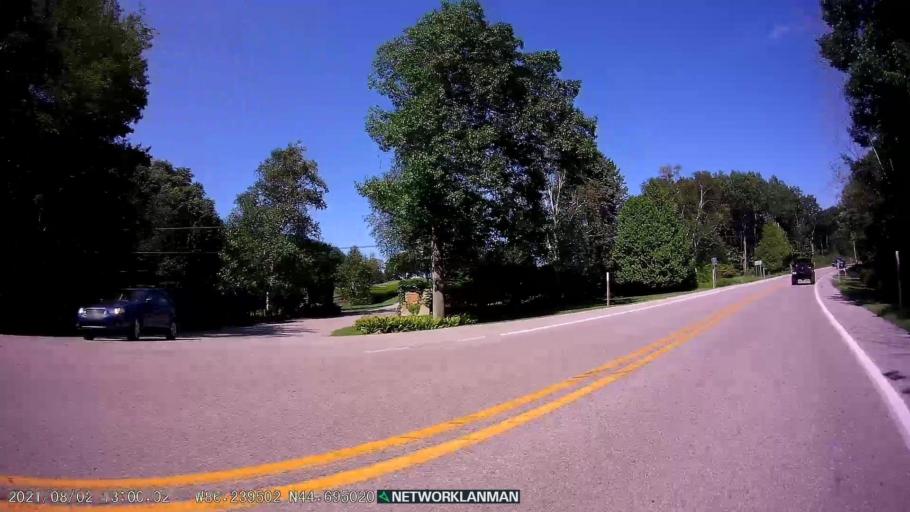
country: US
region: Michigan
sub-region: Benzie County
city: Frankfort
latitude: 44.6952
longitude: -86.2392
